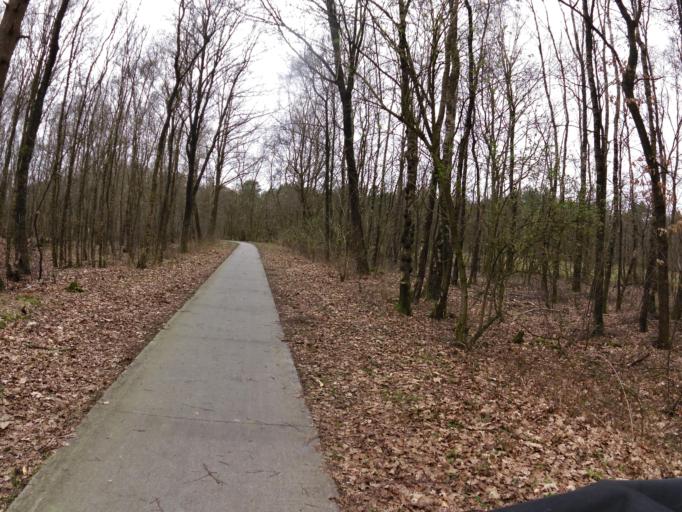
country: NL
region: Drenthe
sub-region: Gemeente Westerveld
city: Dwingeloo
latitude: 52.9806
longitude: 6.3928
